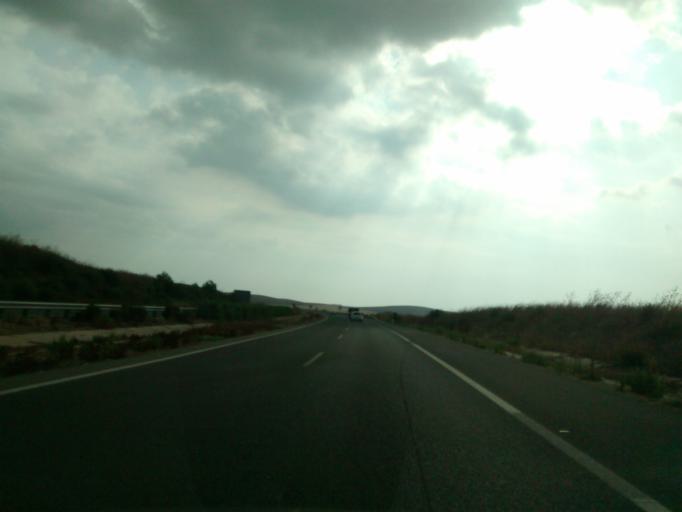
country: ES
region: Andalusia
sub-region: Provincia de Cadiz
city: Arcos de la Frontera
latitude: 36.7660
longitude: -5.8497
